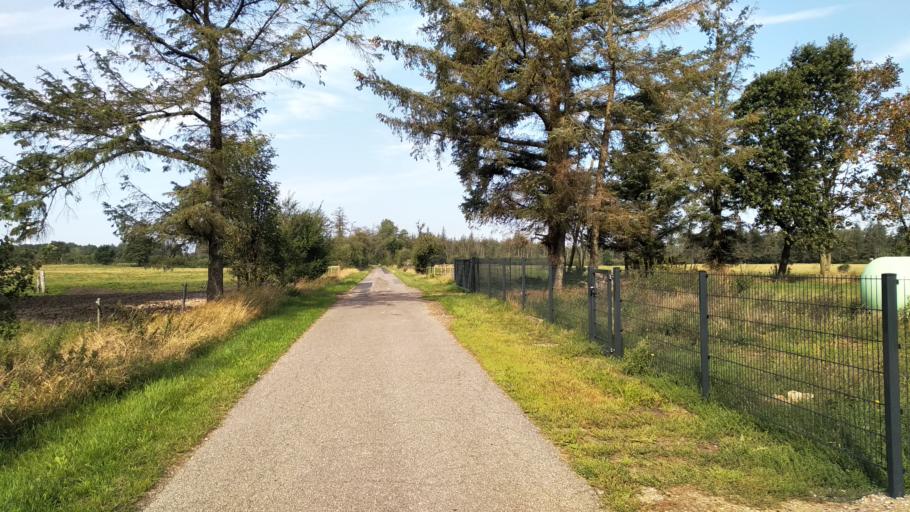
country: DE
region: Schleswig-Holstein
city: Bredstedt
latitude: 54.6465
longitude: 8.9669
